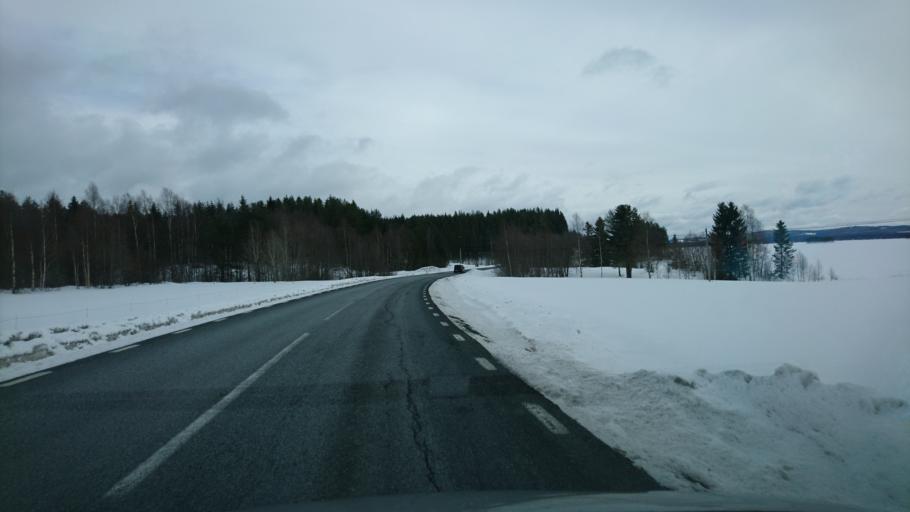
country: SE
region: Vaesternorrland
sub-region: Solleftea Kommun
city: Solleftea
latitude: 63.0598
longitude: 17.0330
